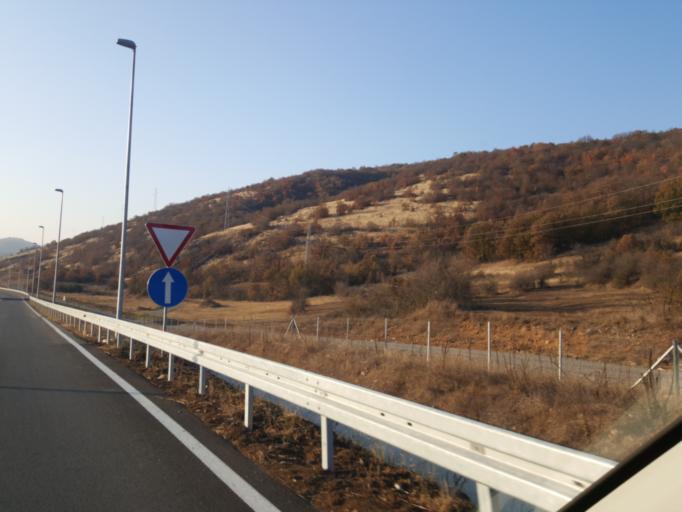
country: RS
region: Central Serbia
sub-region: Pirotski Okrug
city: Dimitrovgrad
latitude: 43.0200
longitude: 22.7453
